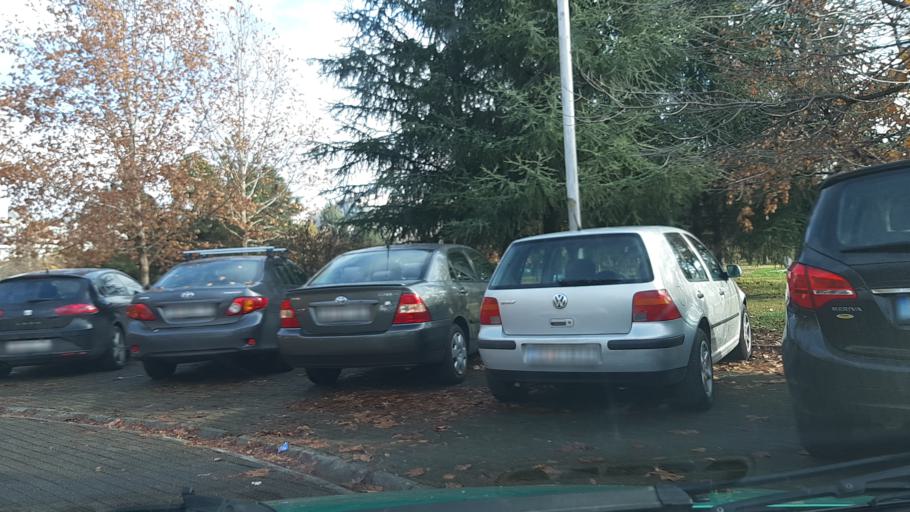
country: MK
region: Kisela Voda
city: Usje
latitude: 41.9879
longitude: 21.4697
